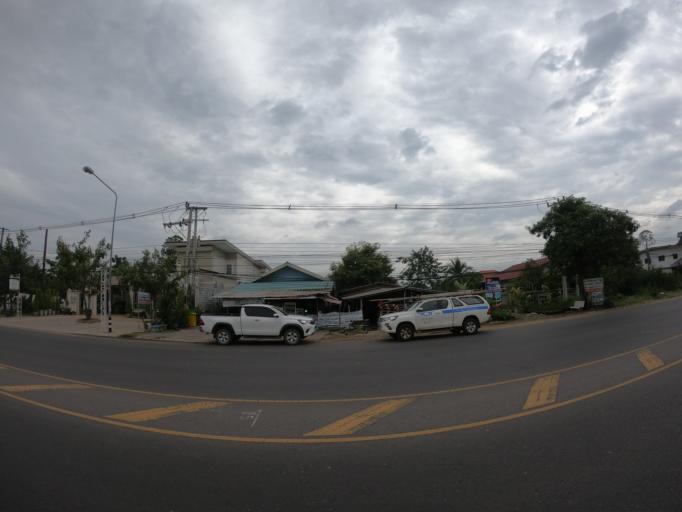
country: TH
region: Roi Et
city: Roi Et
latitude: 16.0649
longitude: 103.6688
